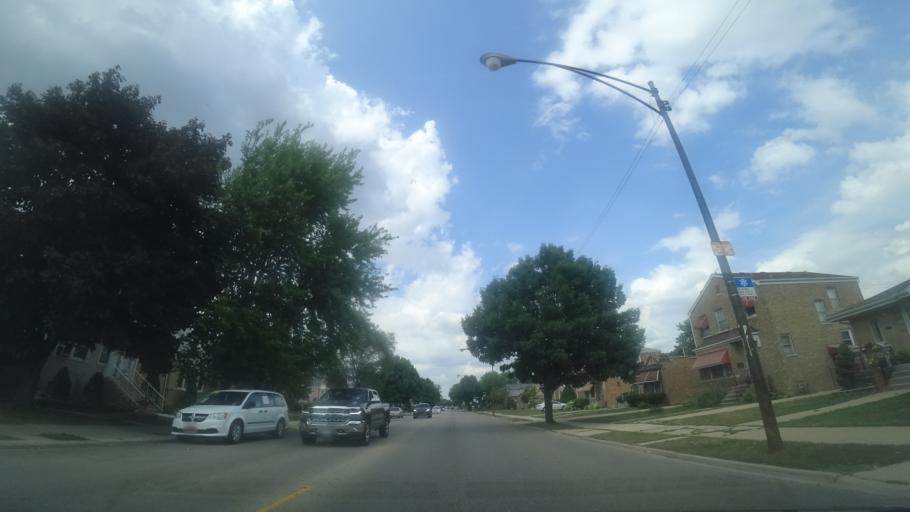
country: US
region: Illinois
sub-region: Cook County
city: Harwood Heights
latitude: 41.9728
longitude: -87.7879
